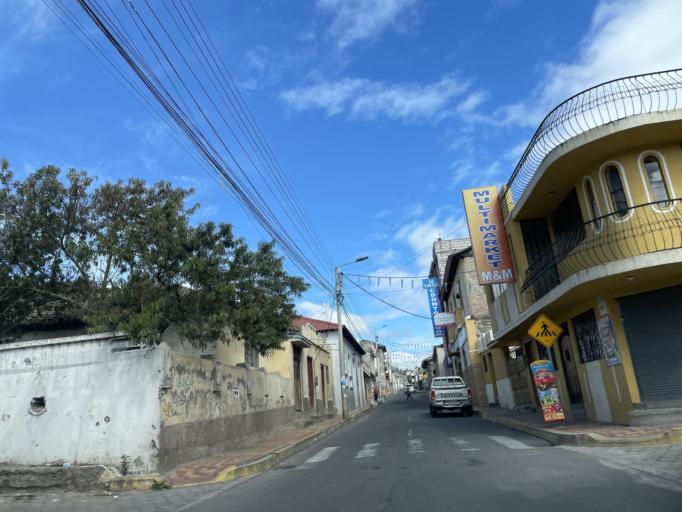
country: EC
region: Chimborazo
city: Guano
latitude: -1.6076
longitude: -78.6388
